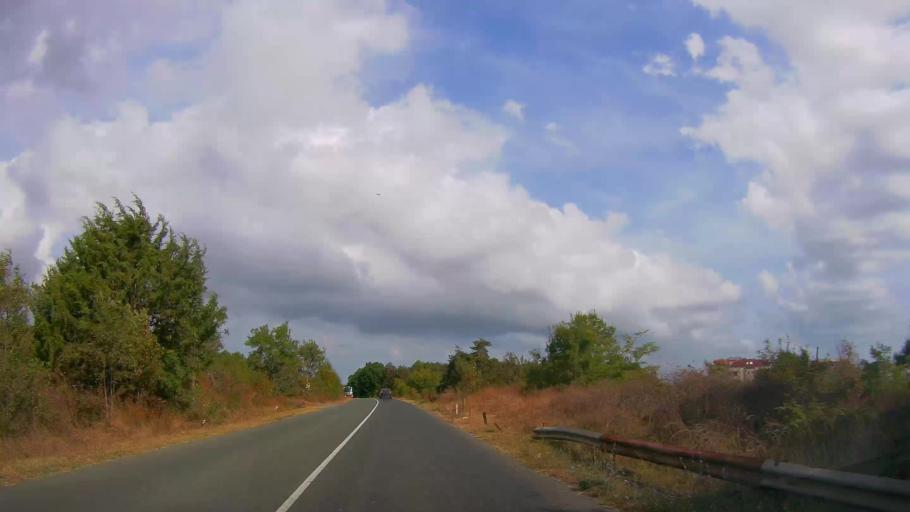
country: BG
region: Burgas
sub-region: Obshtina Primorsko
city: Primorsko
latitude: 42.2705
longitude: 27.7423
